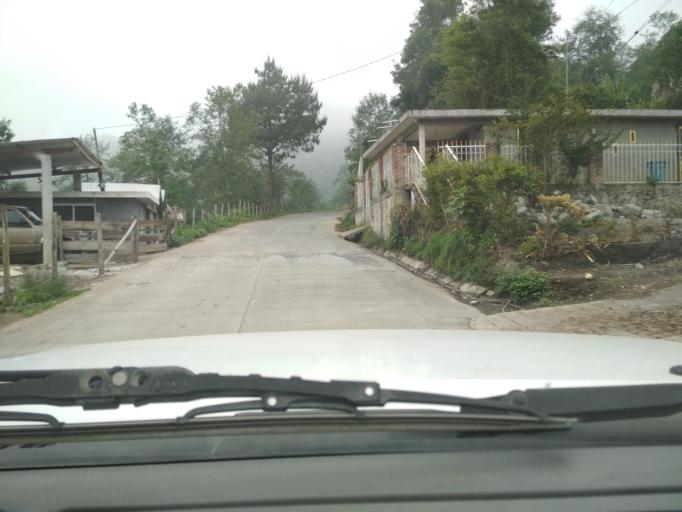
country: MX
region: Veracruz
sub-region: La Perla
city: Chilapa
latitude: 18.9727
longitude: -97.1639
